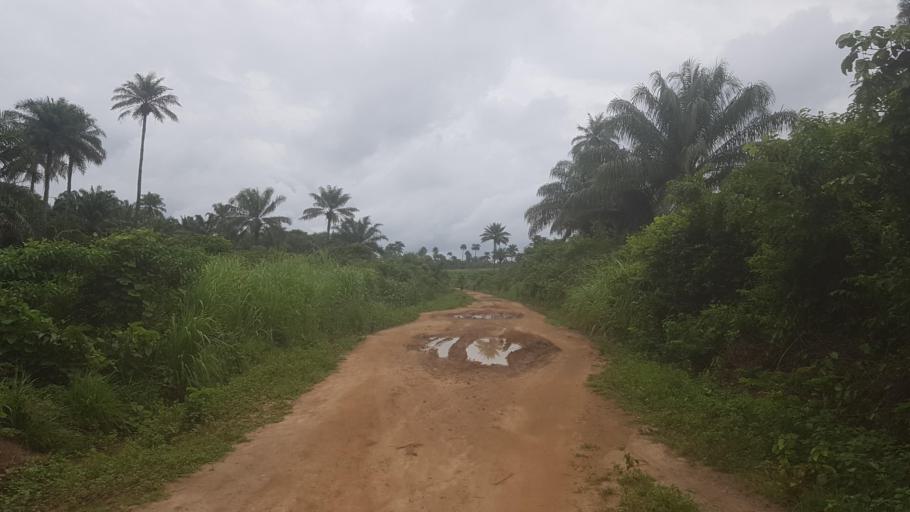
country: SL
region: Southern Province
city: Sumbuya
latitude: 7.5434
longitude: -12.1683
